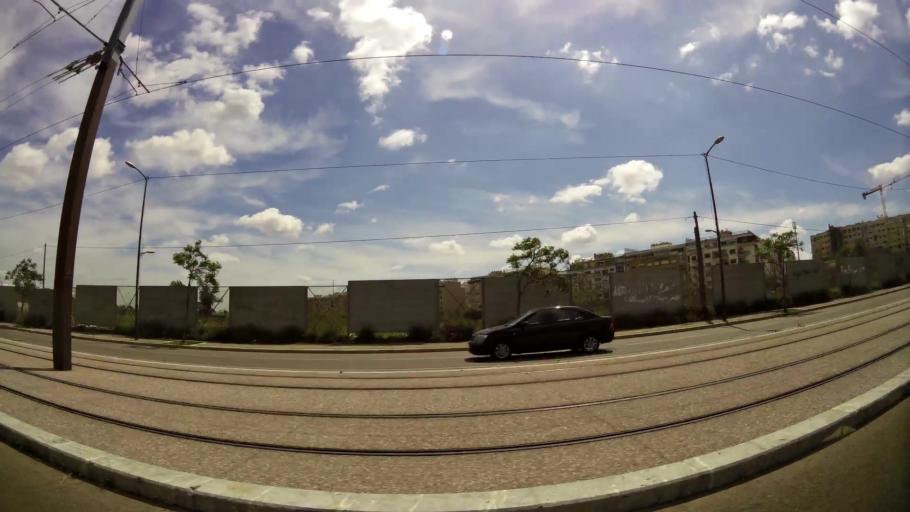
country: MA
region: Grand Casablanca
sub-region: Casablanca
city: Casablanca
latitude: 33.5569
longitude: -7.6304
